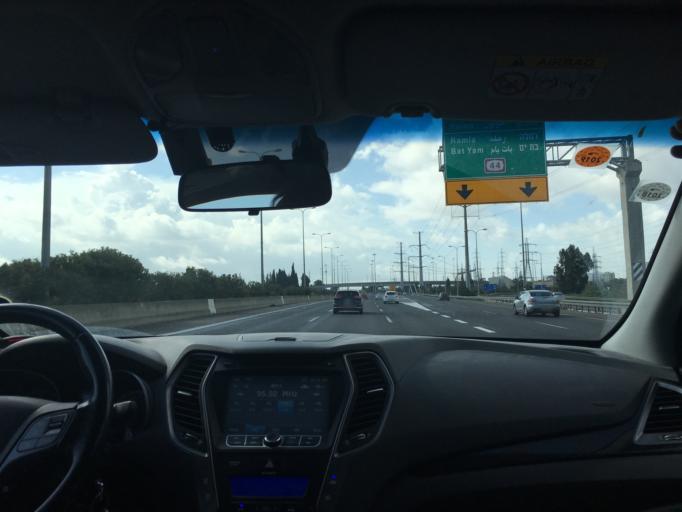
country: IL
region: Tel Aviv
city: Azor
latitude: 32.0251
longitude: 34.8260
